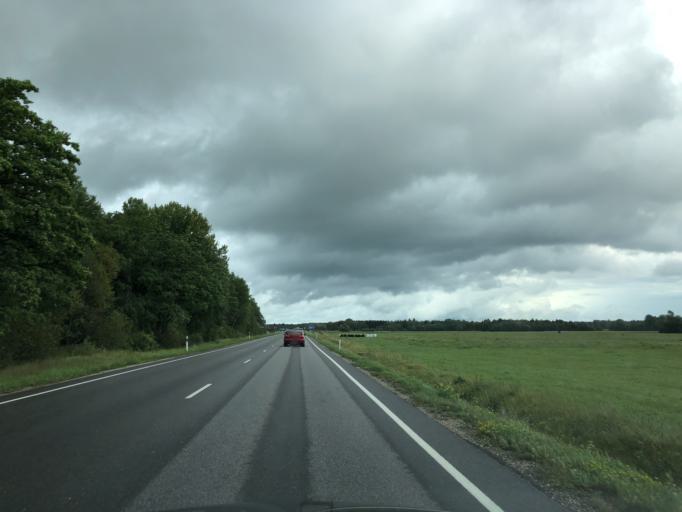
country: EE
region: Laeaene
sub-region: Ridala Parish
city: Uuemoisa
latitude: 58.9662
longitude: 23.8316
